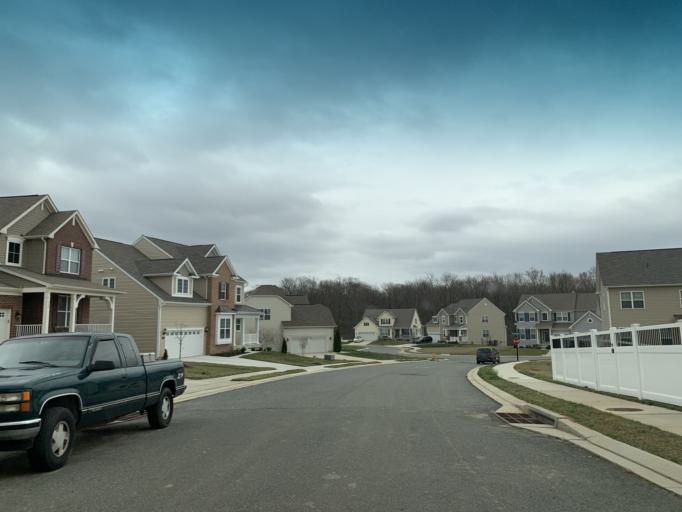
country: US
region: Maryland
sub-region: Harford County
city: Perryman
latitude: 39.4981
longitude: -76.2062
